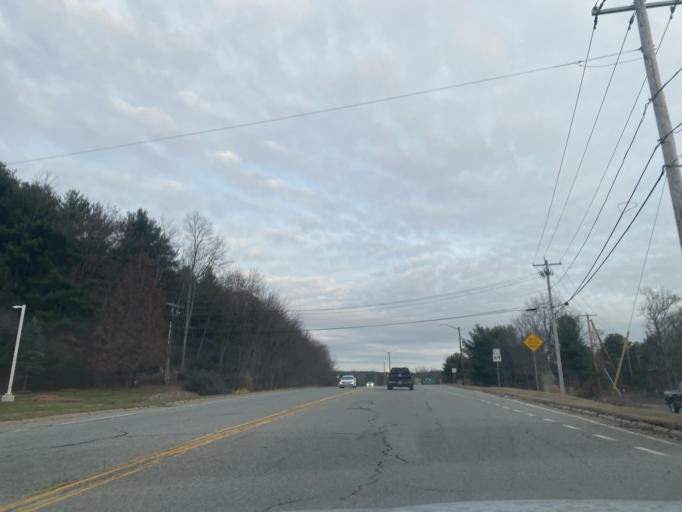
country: US
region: Massachusetts
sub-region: Worcester County
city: East Brookfield
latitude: 42.2316
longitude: -72.0227
